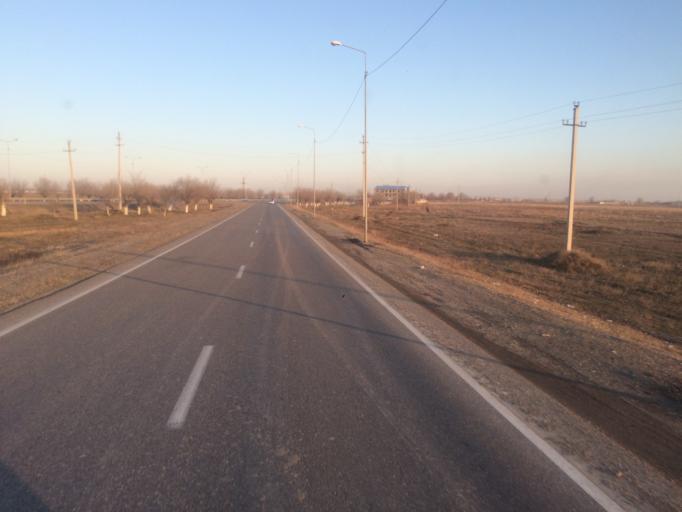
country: KZ
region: Ongtustik Qazaqstan
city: Turkestan
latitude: 43.2734
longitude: 68.3385
